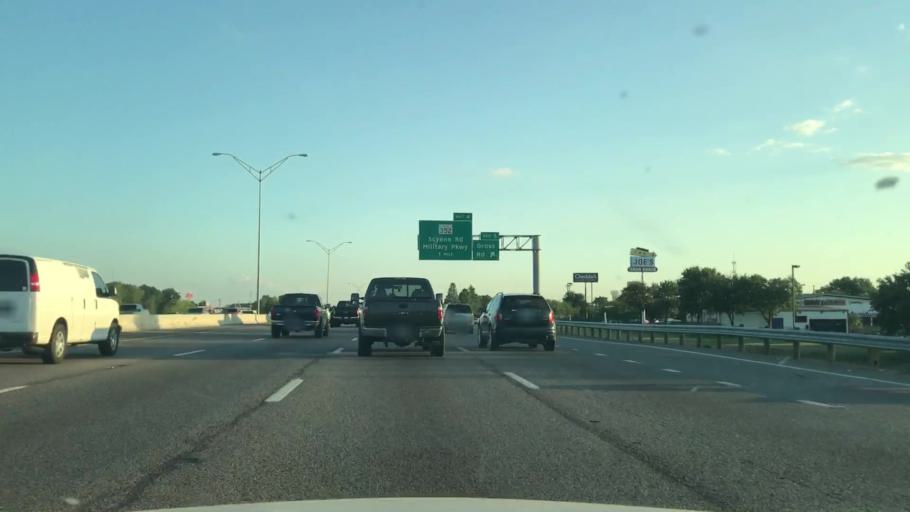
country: US
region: Texas
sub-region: Dallas County
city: Mesquite
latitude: 32.7856
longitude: -96.6246
